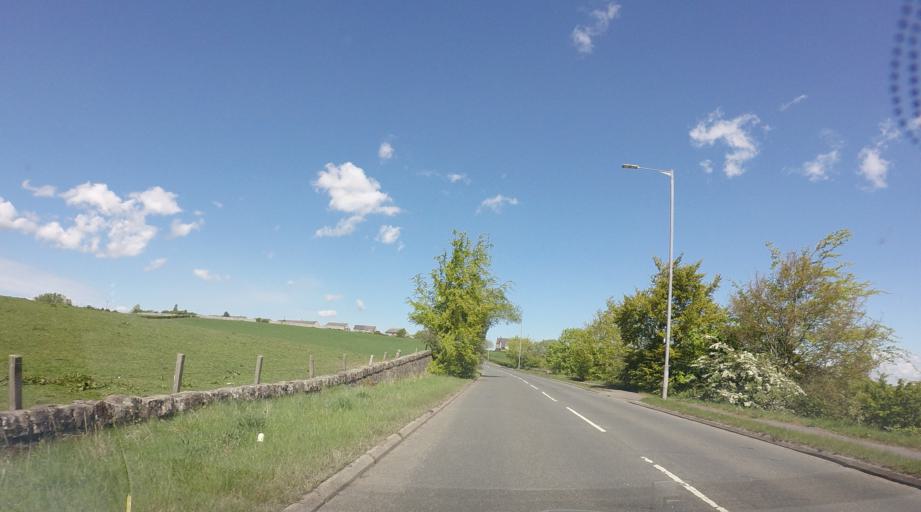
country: GB
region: Scotland
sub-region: Falkirk
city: Polmont
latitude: 55.9647
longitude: -3.6937
